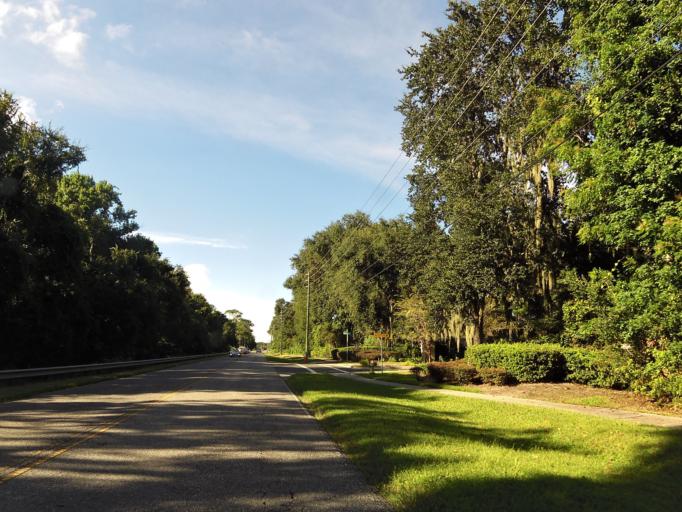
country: US
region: Florida
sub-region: Nassau County
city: Fernandina Beach
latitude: 30.6329
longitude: -81.4554
